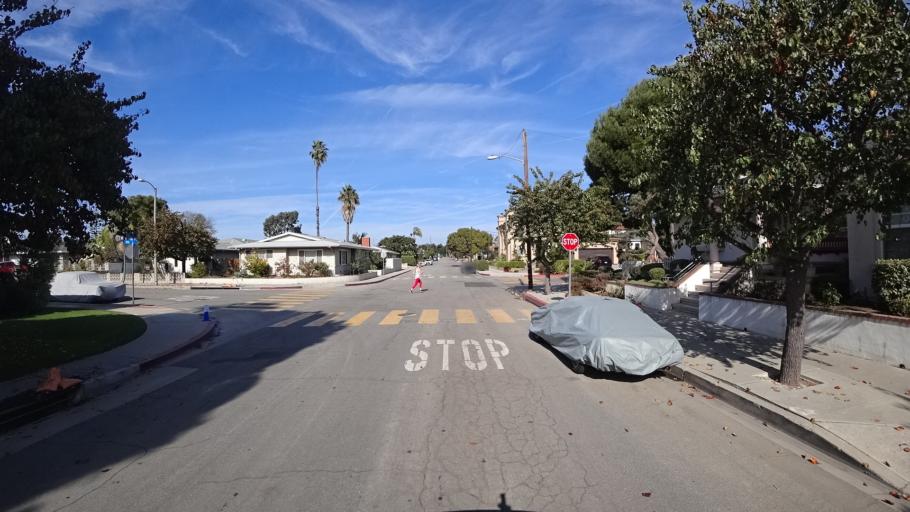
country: US
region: California
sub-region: Los Angeles County
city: Manhattan Beach
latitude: 33.8917
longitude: -118.3852
